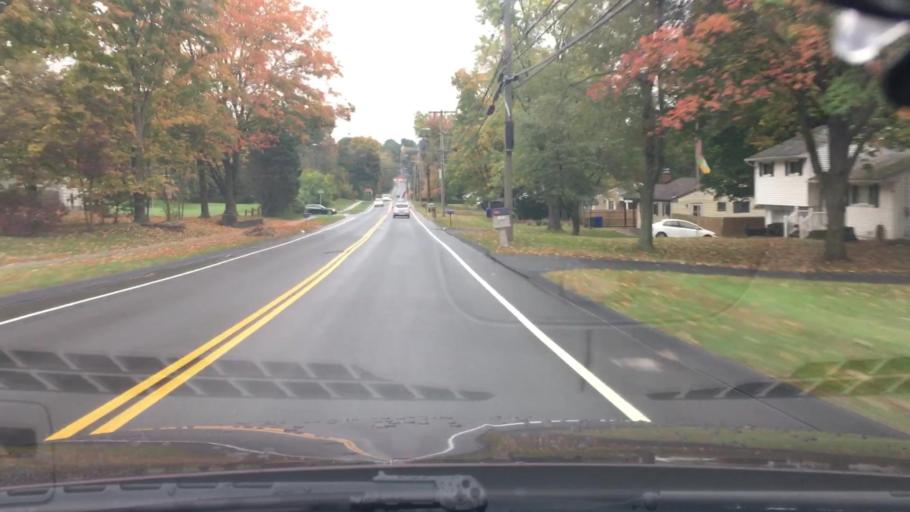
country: US
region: Connecticut
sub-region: Hartford County
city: Manchester
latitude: 41.8246
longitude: -72.5191
